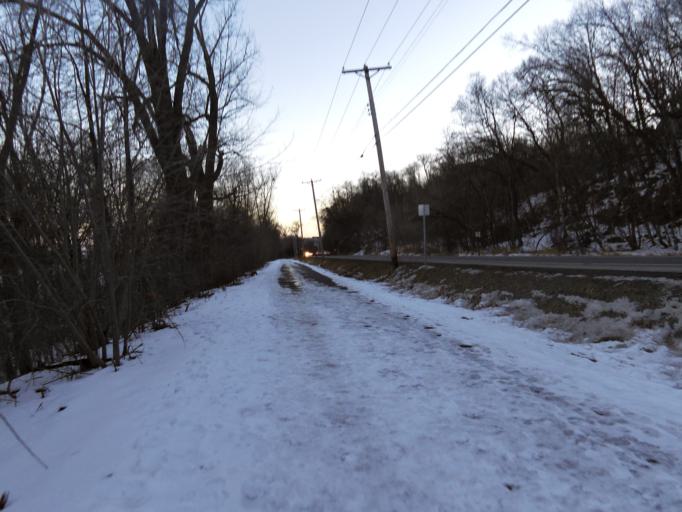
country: US
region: Minnesota
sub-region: Washington County
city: Stillwater
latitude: 45.0690
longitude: -92.8060
